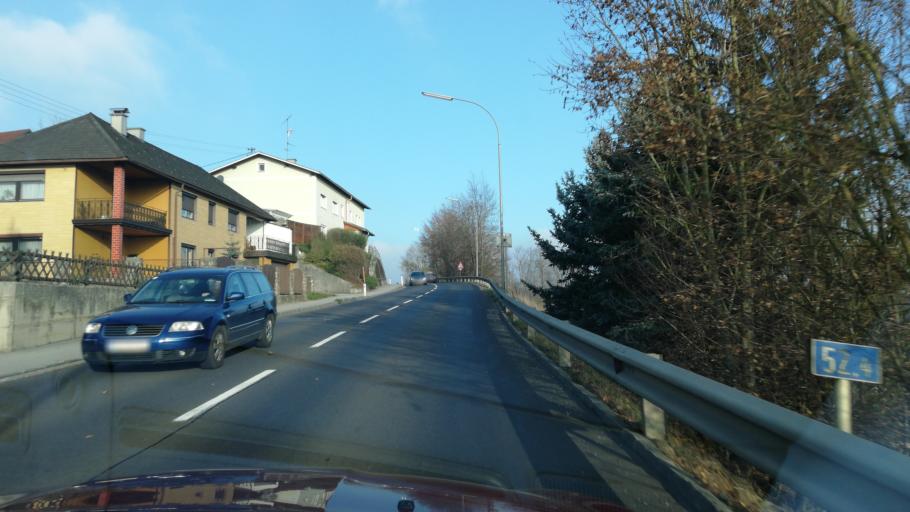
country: AT
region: Upper Austria
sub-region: Politischer Bezirk Steyr-Land
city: Bad Hall
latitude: 48.0546
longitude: 14.2011
